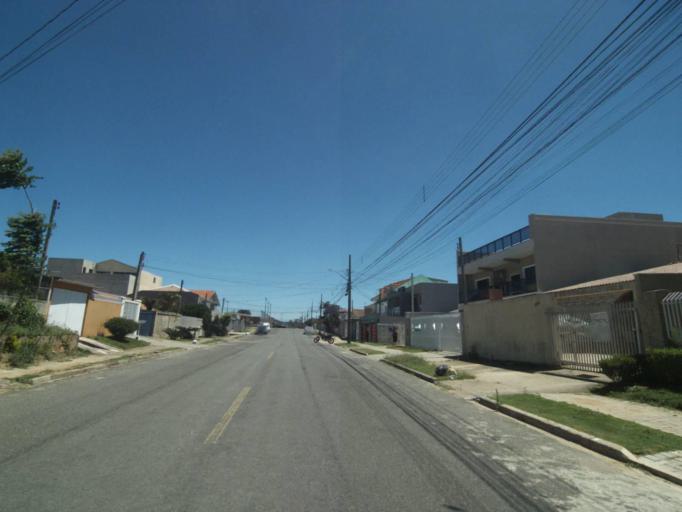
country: BR
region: Parana
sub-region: Curitiba
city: Curitiba
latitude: -25.4778
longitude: -49.3478
